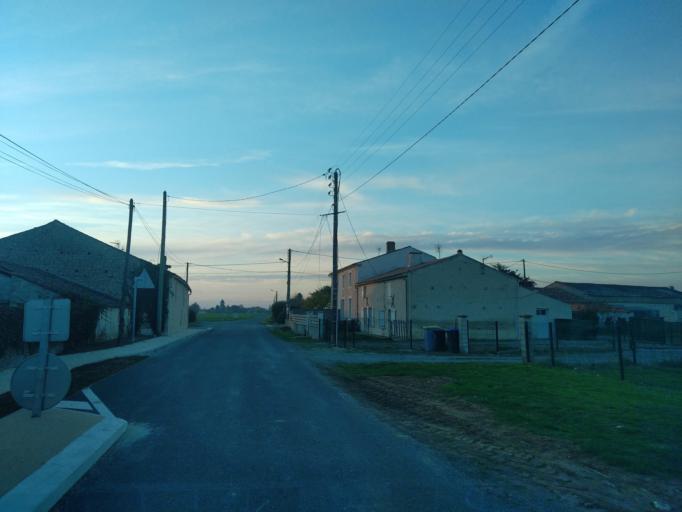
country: FR
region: Pays de la Loire
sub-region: Departement de la Vendee
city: Vix
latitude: 46.3966
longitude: -0.8317
